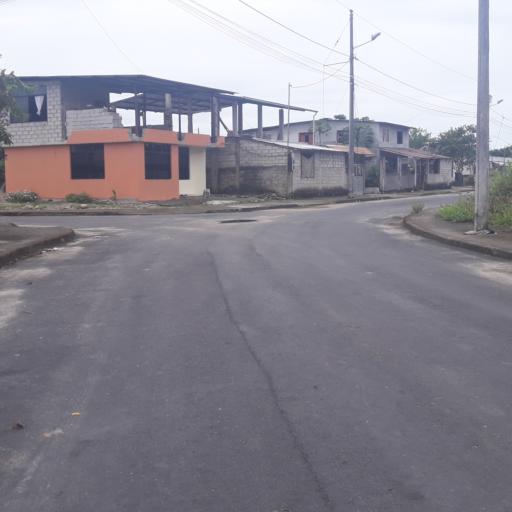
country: EC
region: Napo
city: Tena
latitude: -0.9868
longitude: -77.8325
